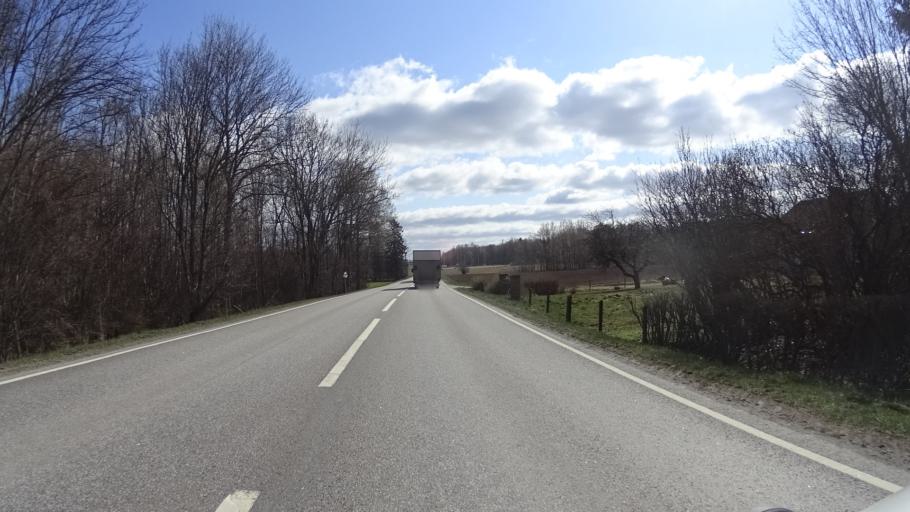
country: SE
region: OEstergoetland
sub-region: Mjolby Kommun
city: Mantorp
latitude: 58.3766
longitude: 15.2753
